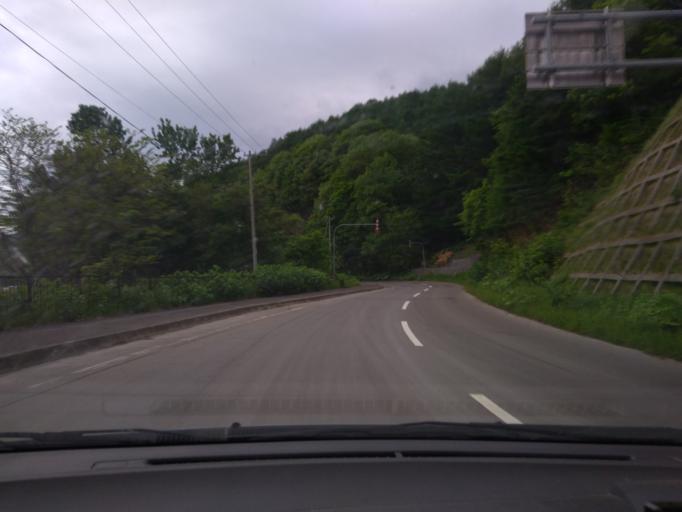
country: JP
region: Hokkaido
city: Shimo-furano
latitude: 43.1586
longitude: 142.5101
